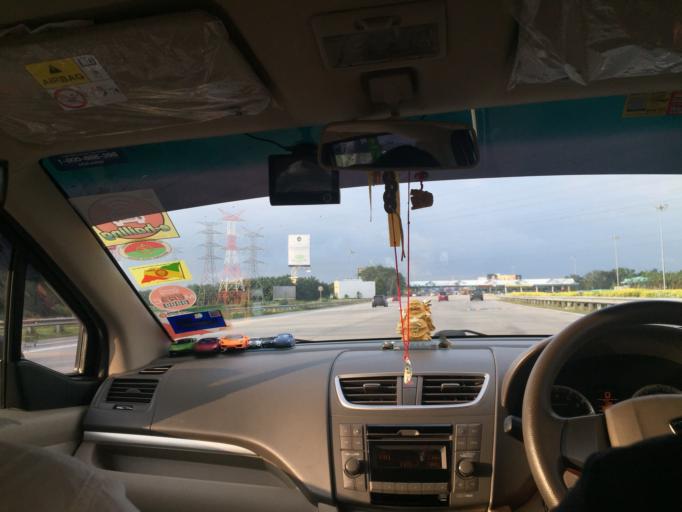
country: MY
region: Putrajaya
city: Putrajaya
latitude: 2.8287
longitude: 101.6605
